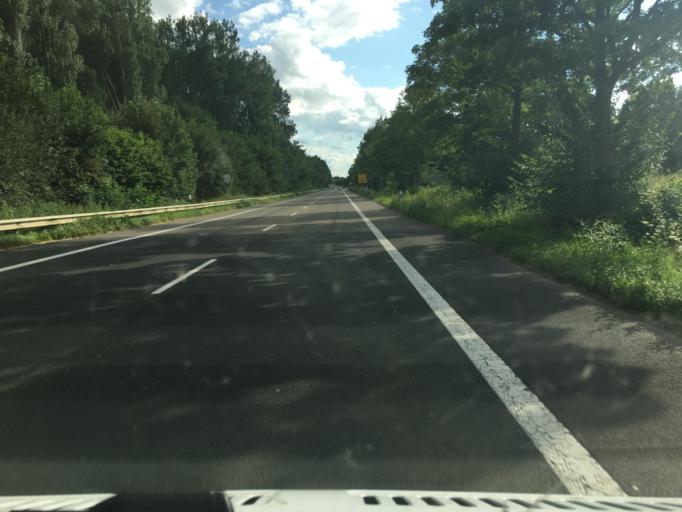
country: DE
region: North Rhine-Westphalia
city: Zulpich
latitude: 50.7217
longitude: 6.6594
